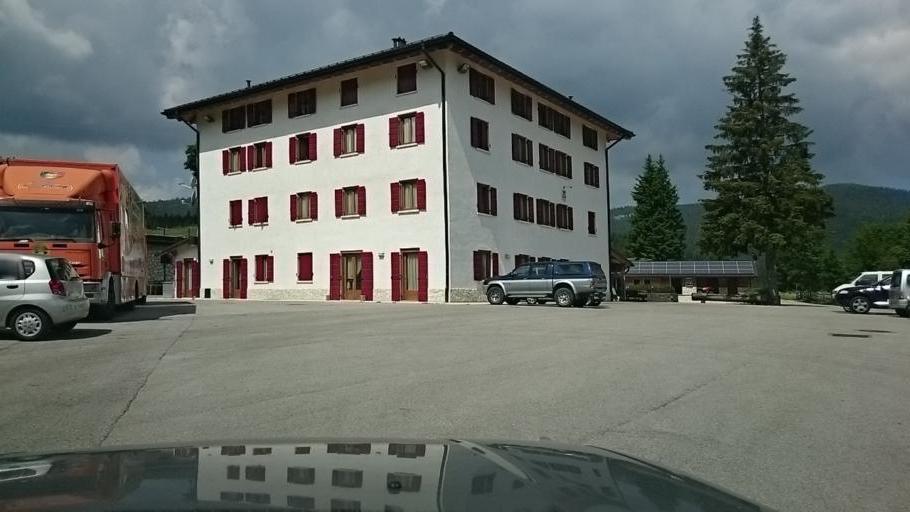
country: IT
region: Trentino-Alto Adige
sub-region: Provincia di Trento
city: Grigno
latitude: 45.9799
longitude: 11.5920
